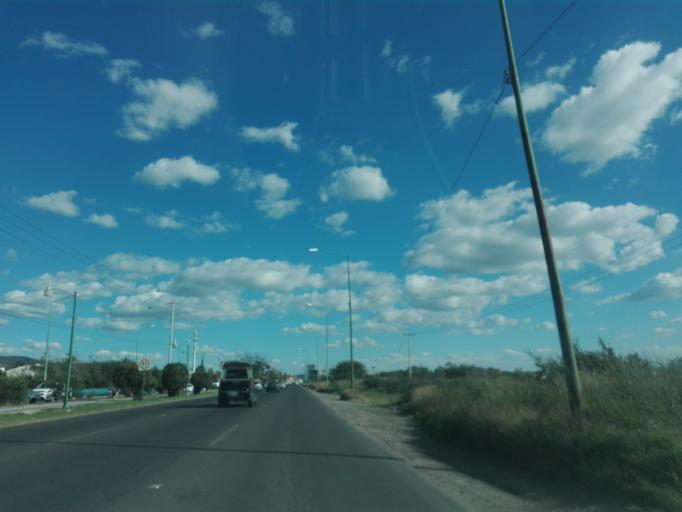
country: MX
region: Guanajuato
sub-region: Leon
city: Medina
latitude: 21.1556
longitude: -101.6405
